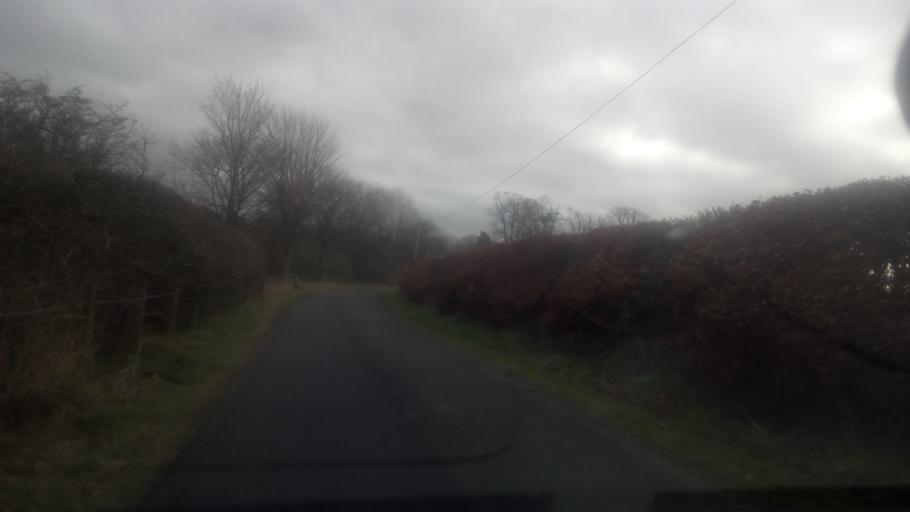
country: GB
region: Scotland
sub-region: The Scottish Borders
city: Kelso
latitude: 55.5415
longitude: -2.4660
